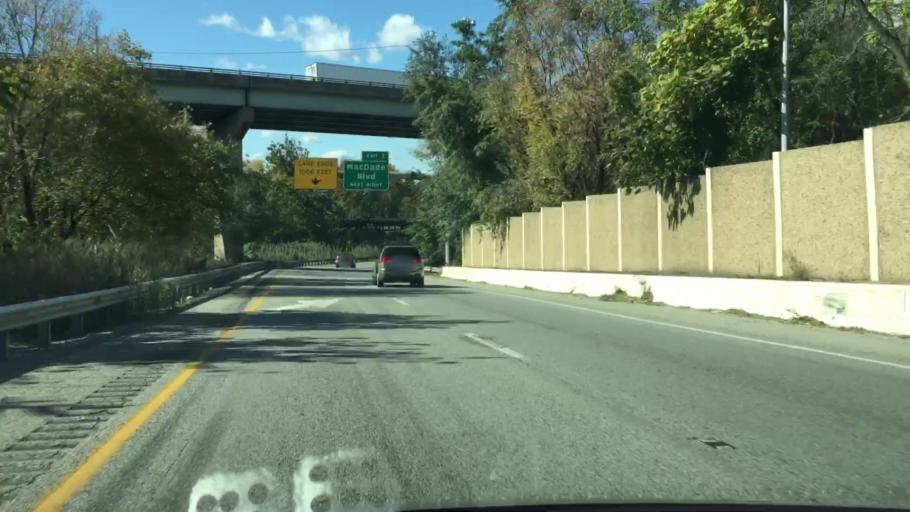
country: US
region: Pennsylvania
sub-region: Delaware County
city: Woodlyn
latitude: 39.8686
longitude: -75.3422
